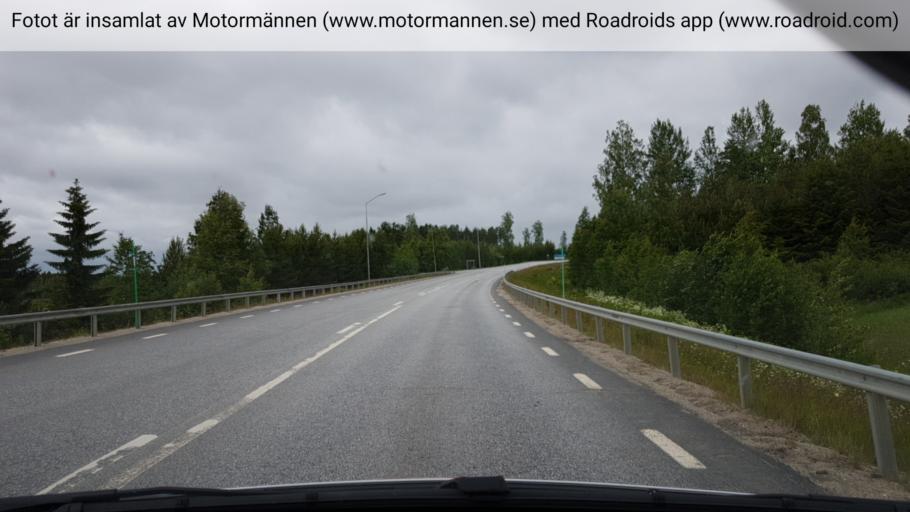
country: SE
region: Vaesterbotten
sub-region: Vannas Kommun
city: Vaennaes
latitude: 63.9834
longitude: 19.7292
